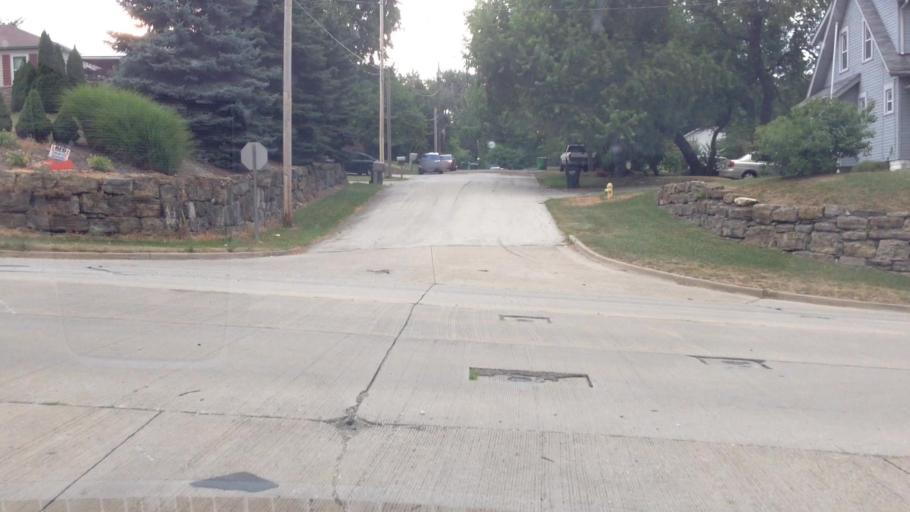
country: US
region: Ohio
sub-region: Summit County
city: Barberton
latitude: 41.0382
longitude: -81.5825
